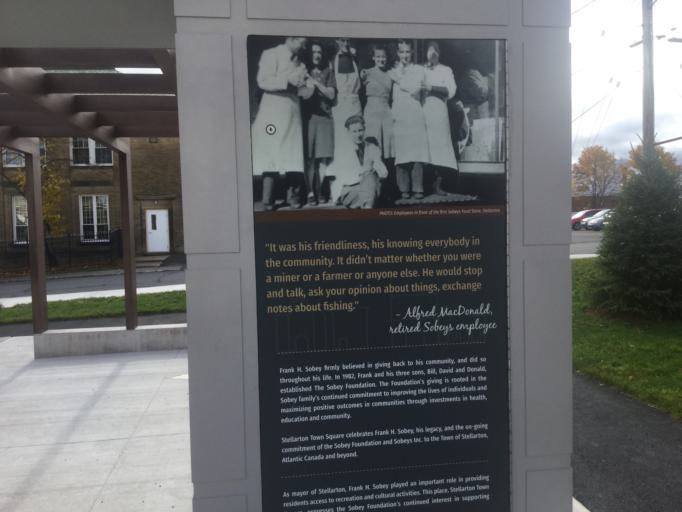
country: CA
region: Nova Scotia
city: New Glasgow
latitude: 45.5597
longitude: -62.6603
